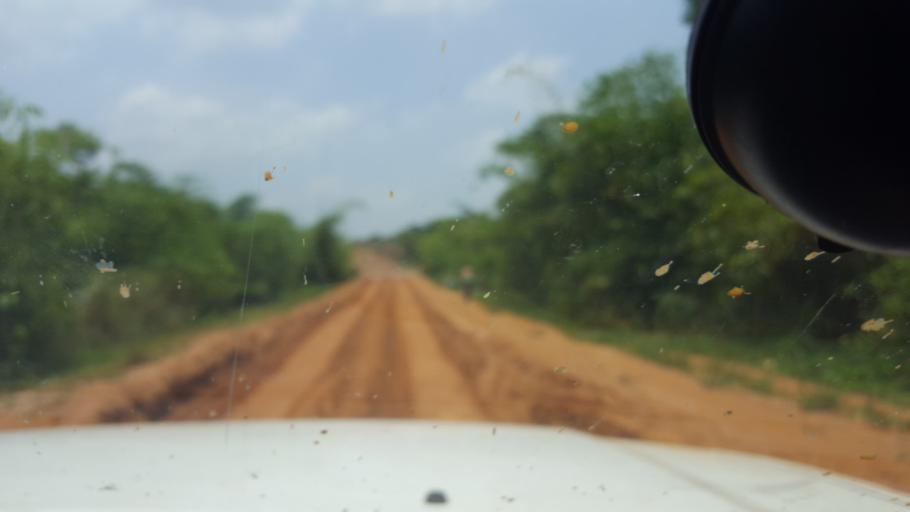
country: CD
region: Bandundu
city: Mushie
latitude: -3.7480
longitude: 16.6590
